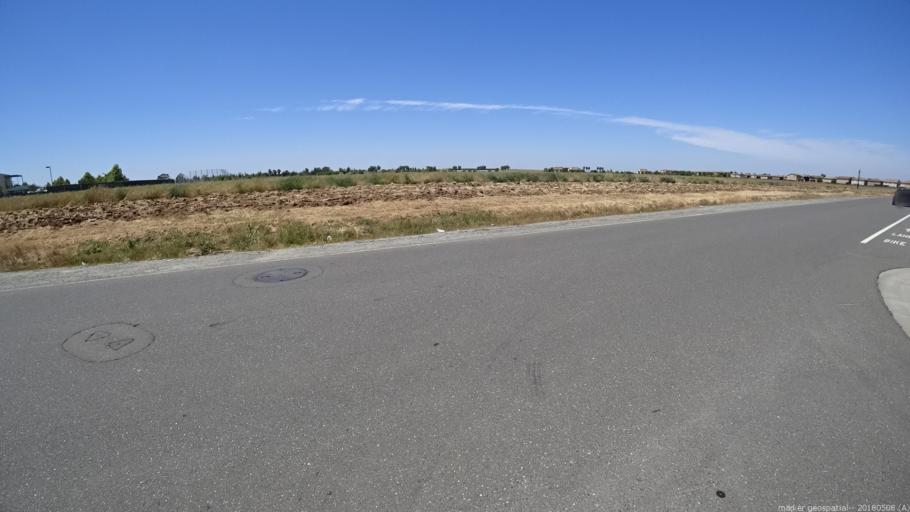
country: US
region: California
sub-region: Sacramento County
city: Elverta
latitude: 38.6681
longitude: -121.5304
